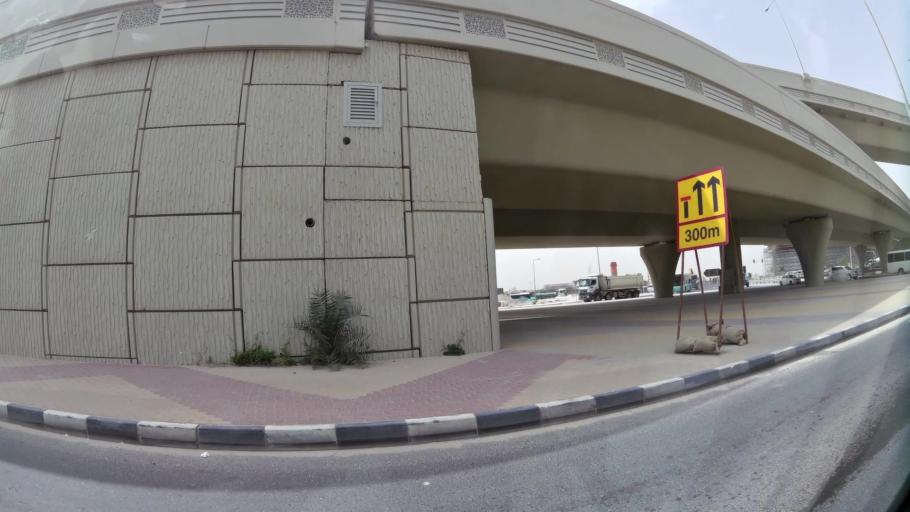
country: QA
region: Baladiyat ad Dawhah
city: Doha
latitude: 25.2953
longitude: 51.4763
